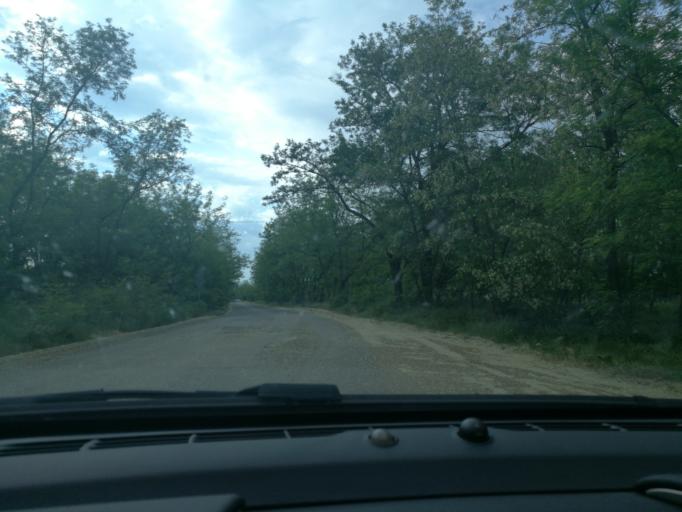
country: HU
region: Szabolcs-Szatmar-Bereg
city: Nyirpazony
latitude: 47.9290
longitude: 21.7984
